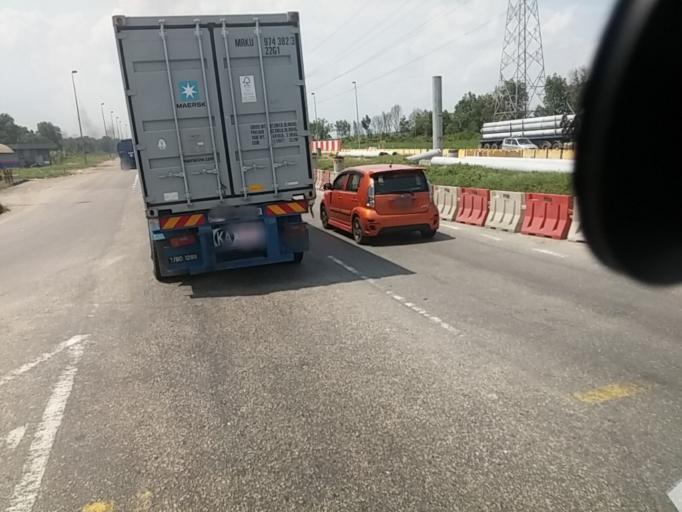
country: MY
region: Selangor
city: Klang
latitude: 2.9703
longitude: 101.3638
